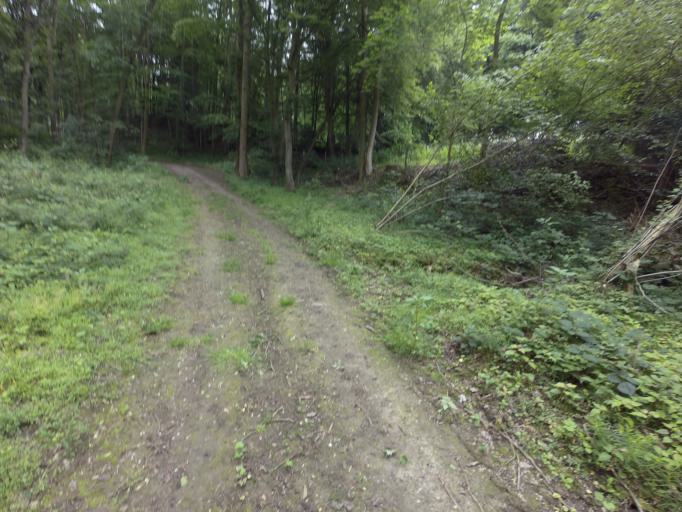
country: NL
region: Limburg
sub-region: Gemeente Simpelveld
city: Simpelveld
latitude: 50.8025
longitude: 5.9730
